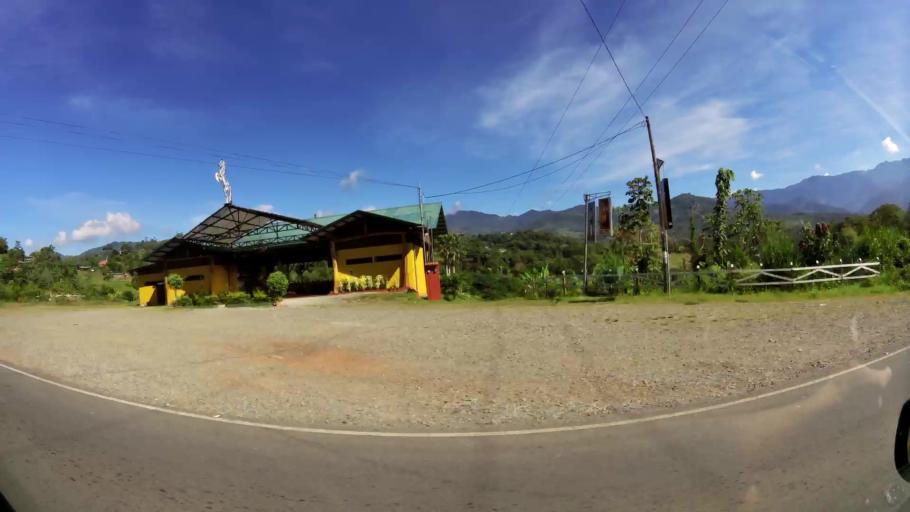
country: CR
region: San Jose
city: San Isidro
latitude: 9.3947
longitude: -83.7124
